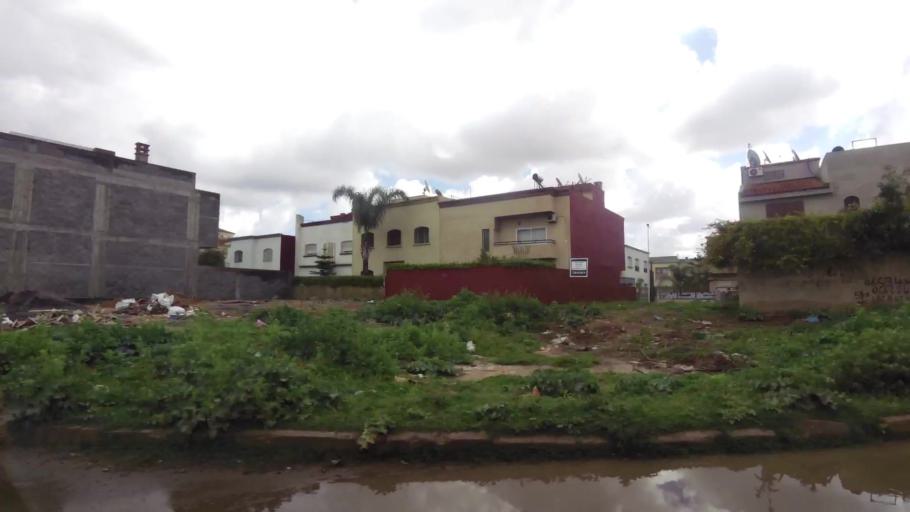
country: MA
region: Grand Casablanca
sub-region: Nouaceur
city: Bouskoura
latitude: 33.5184
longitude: -7.6432
